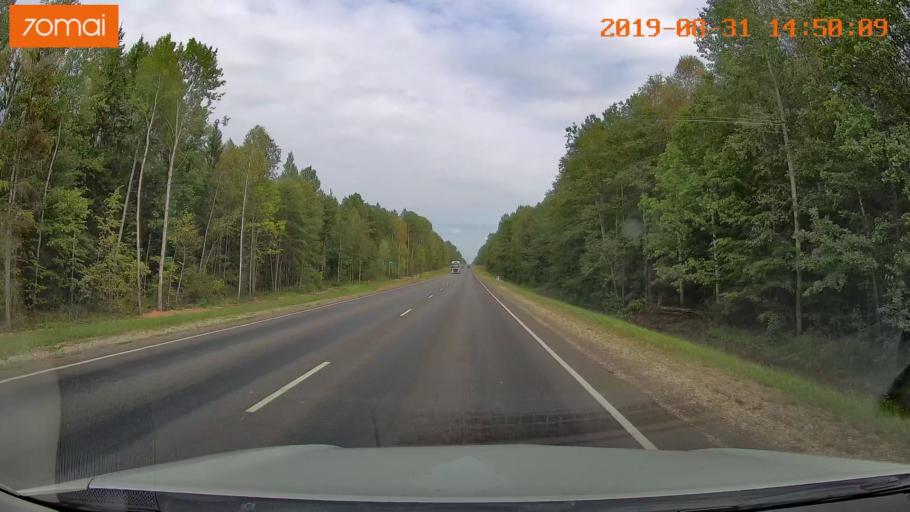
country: RU
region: Kaluga
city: Spas-Demensk
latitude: 54.2593
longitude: 33.7827
